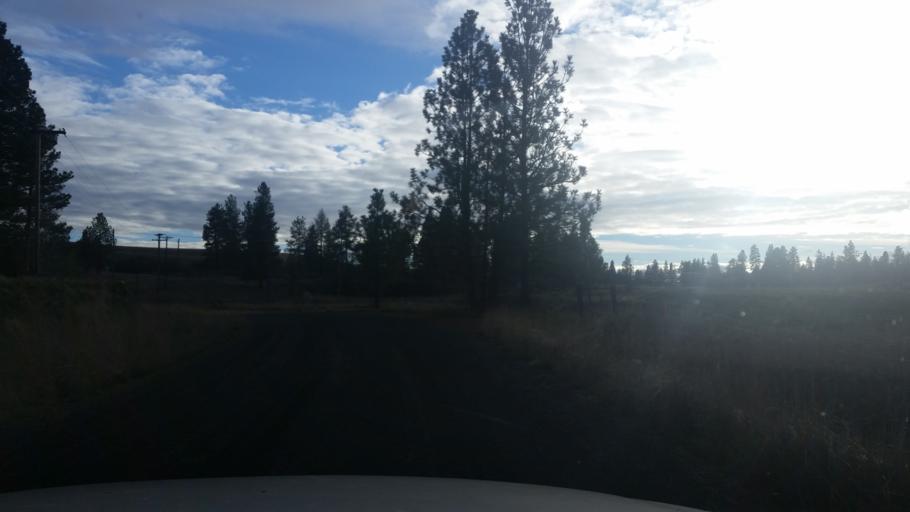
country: US
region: Washington
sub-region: Spokane County
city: Cheney
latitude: 47.4284
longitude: -117.4346
